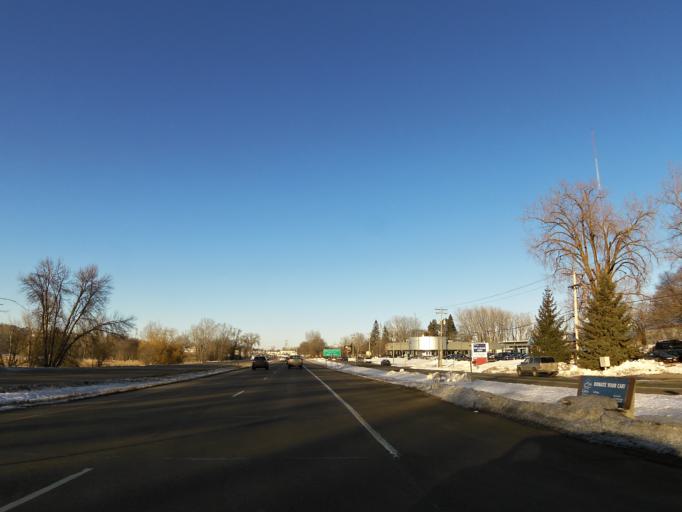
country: US
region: Minnesota
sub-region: Ramsey County
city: Little Canada
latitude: 45.0233
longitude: -93.0492
